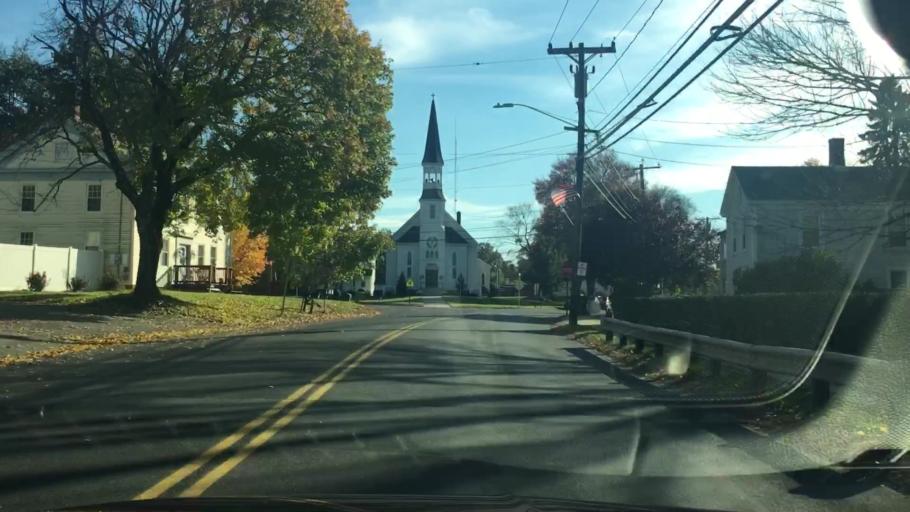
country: US
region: Connecticut
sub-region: Hartford County
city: Broad Brook
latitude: 41.9129
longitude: -72.5454
